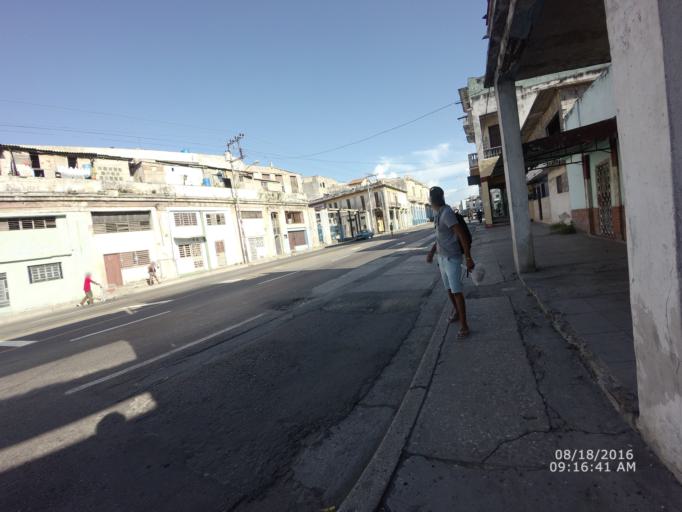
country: CU
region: La Habana
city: Havana
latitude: 23.1298
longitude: -82.3765
